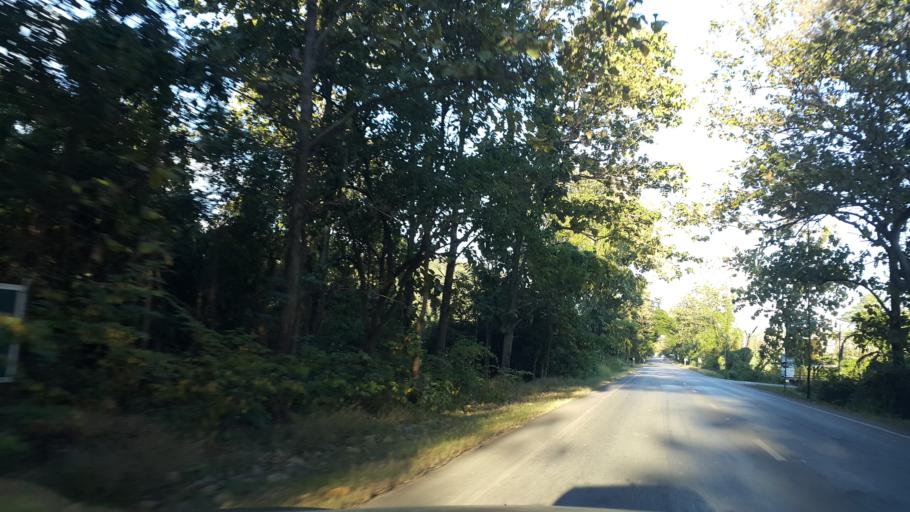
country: TH
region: Sukhothai
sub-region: Amphoe Si Satchanalai
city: Si Satchanalai
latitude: 17.5512
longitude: 99.9018
